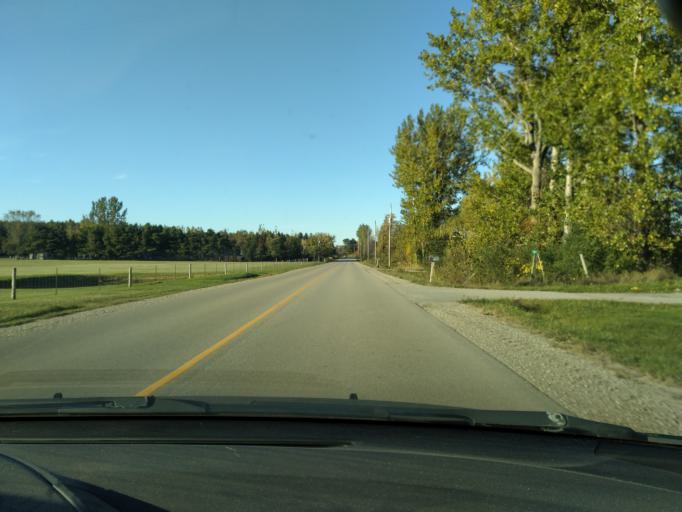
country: CA
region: Ontario
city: Bradford West Gwillimbury
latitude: 44.0153
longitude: -79.7253
